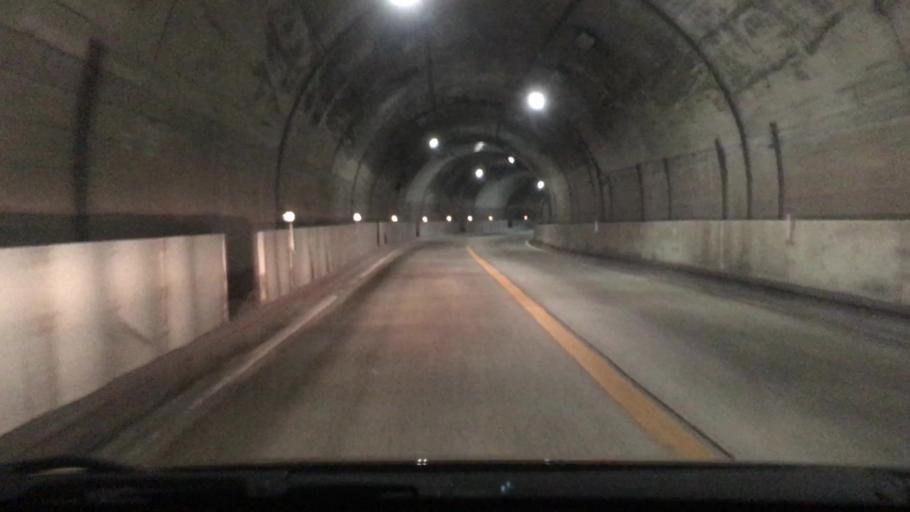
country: JP
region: Nagasaki
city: Togitsu
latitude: 32.8269
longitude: 129.7694
